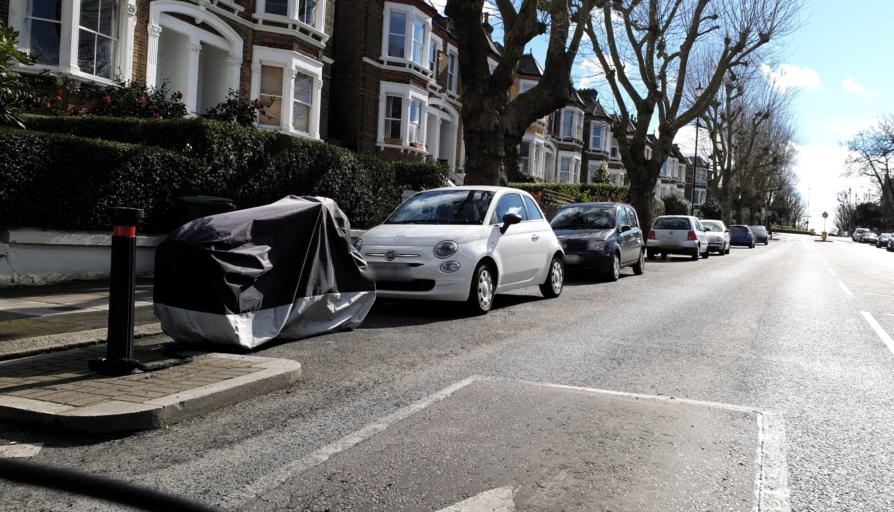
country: GB
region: England
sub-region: Greater London
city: Catford
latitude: 51.4700
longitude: -0.0444
